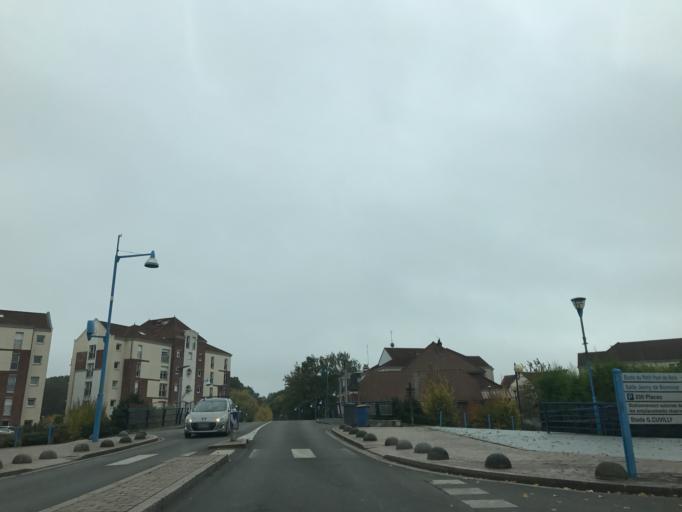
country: FR
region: Nord-Pas-de-Calais
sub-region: Departement du Pas-de-Calais
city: Saint-Laurent-Blangy
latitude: 50.2989
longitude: 2.8024
